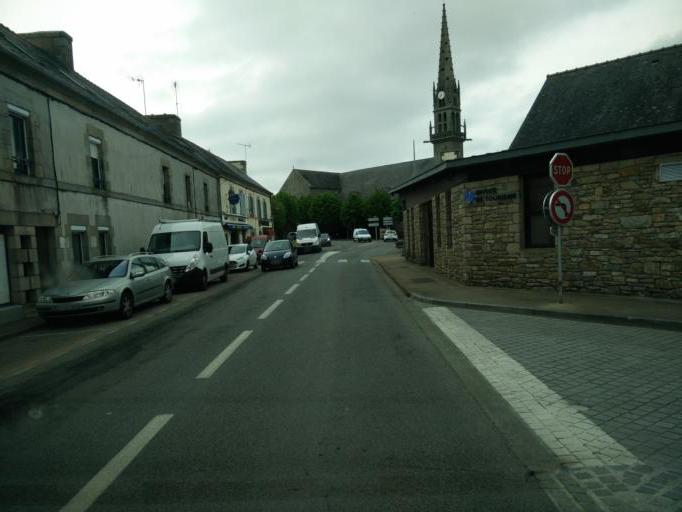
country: FR
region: Brittany
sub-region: Departement du Finistere
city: Tregunc
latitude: 47.8561
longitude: -3.8535
